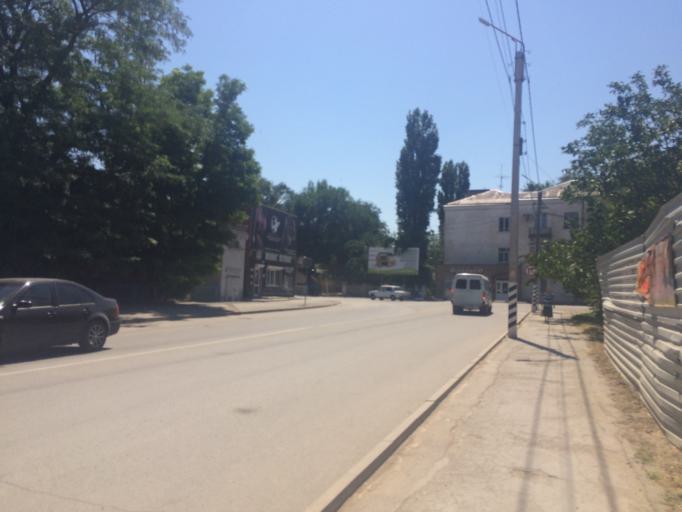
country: RU
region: Rostov
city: Sal'sk
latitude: 46.4710
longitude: 41.5435
